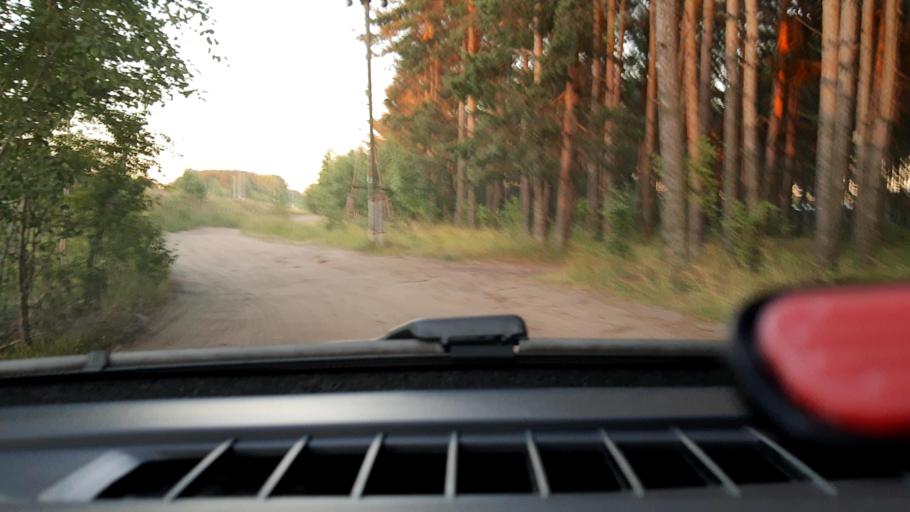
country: RU
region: Nizjnij Novgorod
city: Gorbatovka
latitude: 56.3812
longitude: 43.7725
